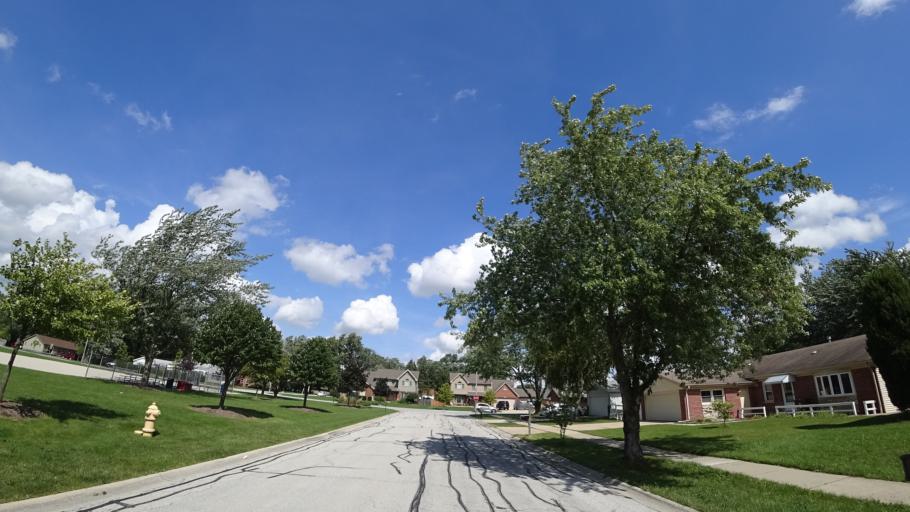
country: US
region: Illinois
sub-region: Cook County
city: Tinley Park
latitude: 41.5654
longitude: -87.7799
